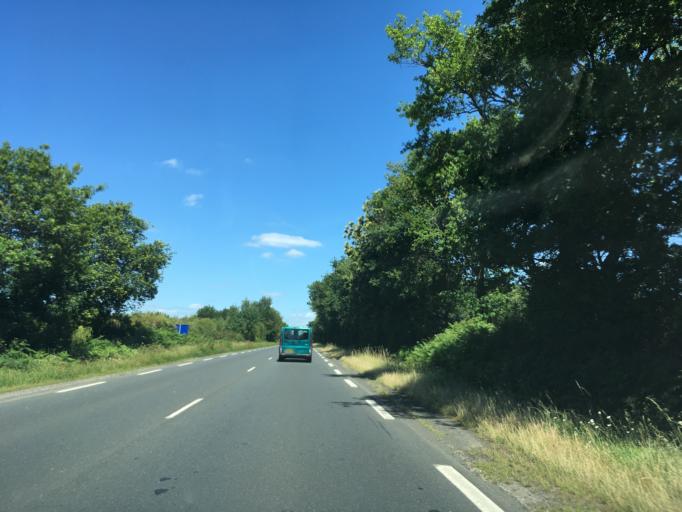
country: FR
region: Pays de la Loire
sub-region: Departement de la Loire-Atlantique
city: Le Bignon
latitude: 47.1249
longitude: -1.4979
